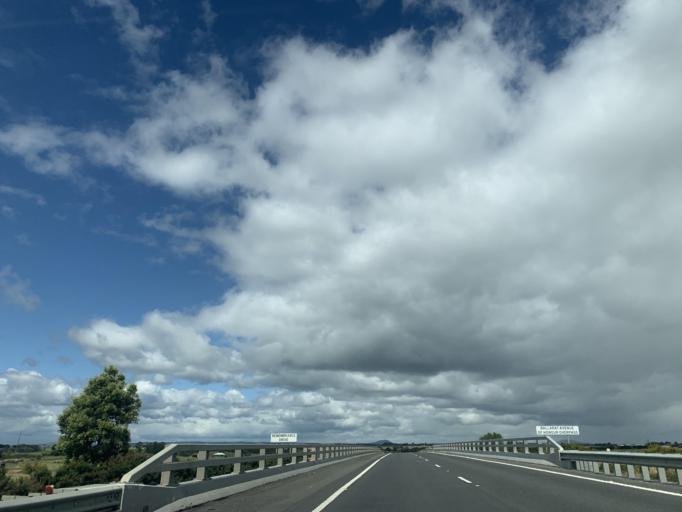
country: AU
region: Victoria
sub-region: Ballarat North
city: Newington
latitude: -37.4758
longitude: 143.6738
